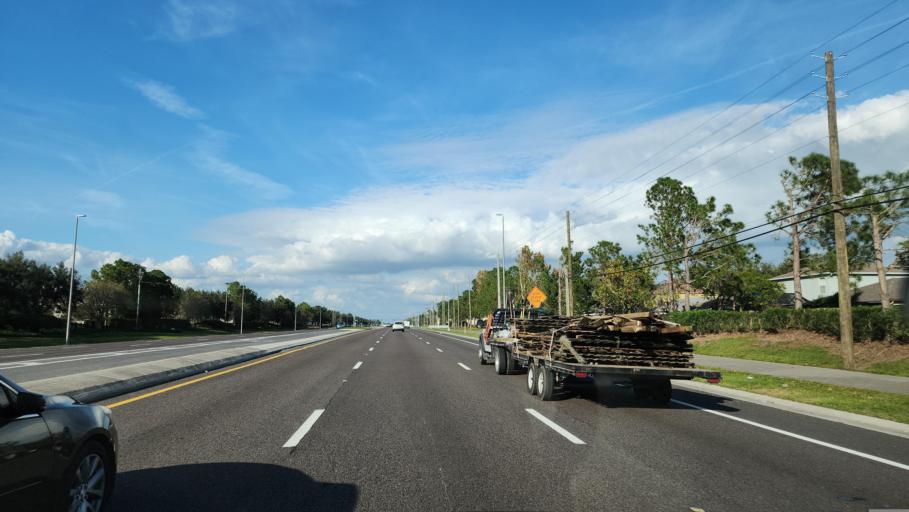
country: US
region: Florida
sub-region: Hillsborough County
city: Riverview
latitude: 27.8065
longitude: -82.3328
